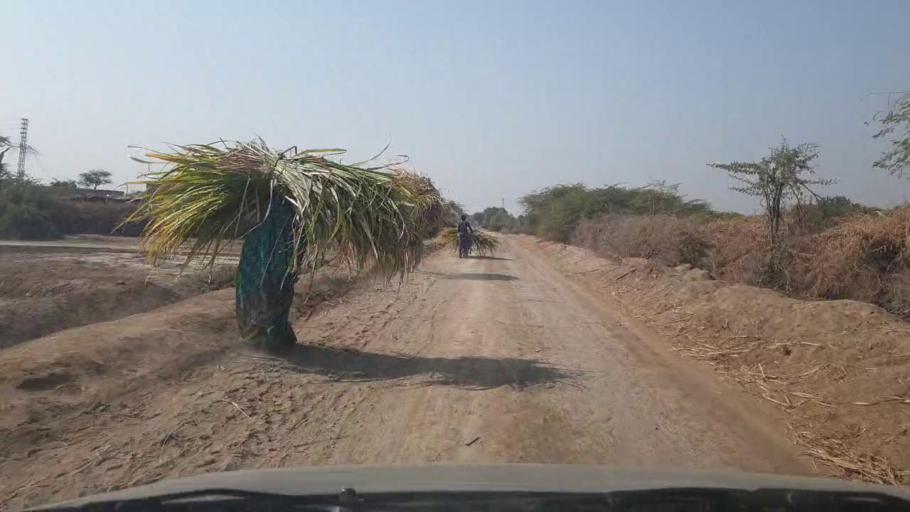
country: PK
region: Sindh
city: Digri
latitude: 25.2350
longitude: 69.0905
